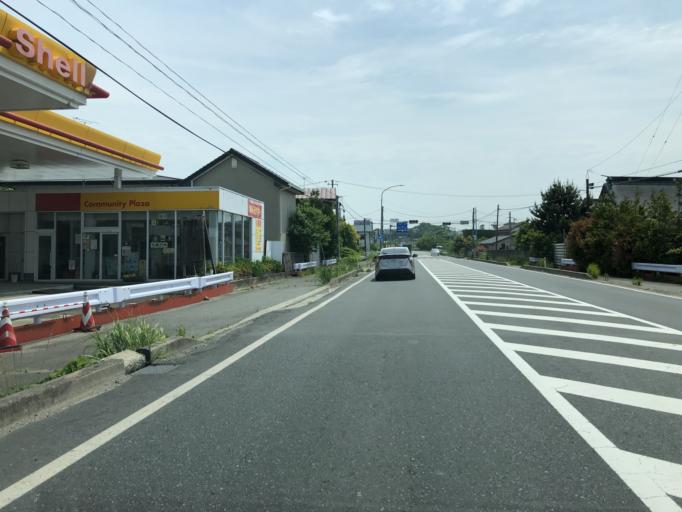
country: JP
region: Fukushima
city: Namie
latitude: 37.4491
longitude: 141.0090
